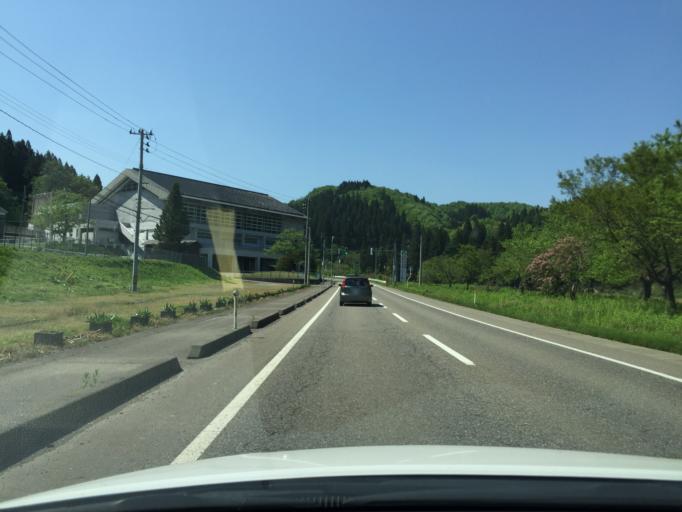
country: JP
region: Niigata
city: Kamo
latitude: 37.6155
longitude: 139.1030
